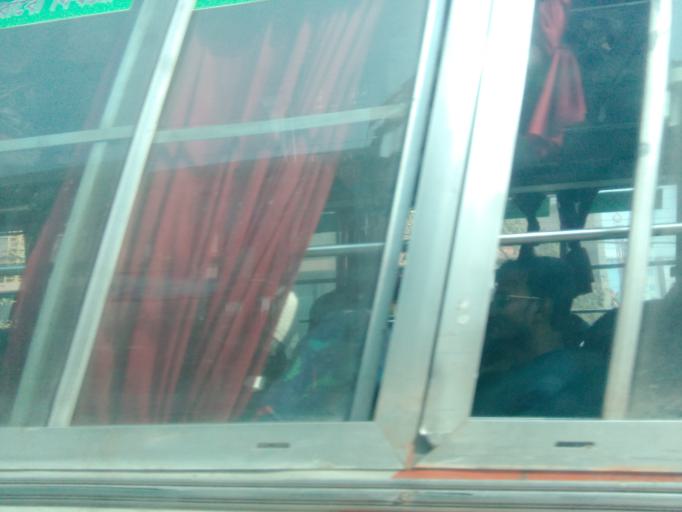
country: BD
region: Dhaka
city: Paltan
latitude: 23.8134
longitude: 90.4212
